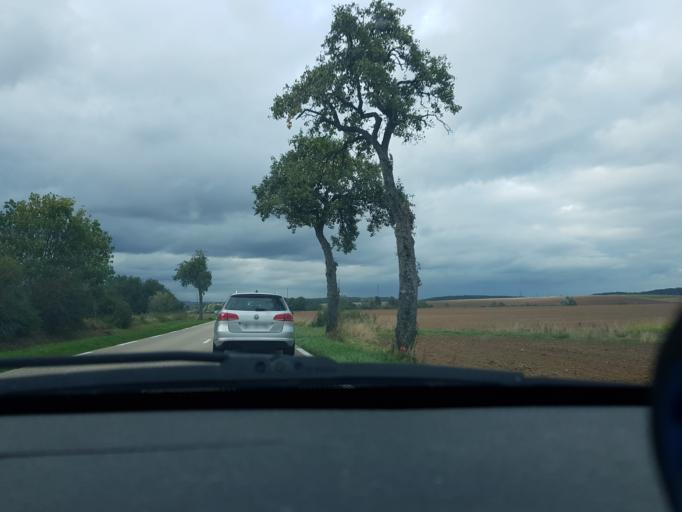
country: FR
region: Lorraine
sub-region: Departement de la Moselle
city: Morhange
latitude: 48.9489
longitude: 6.6110
